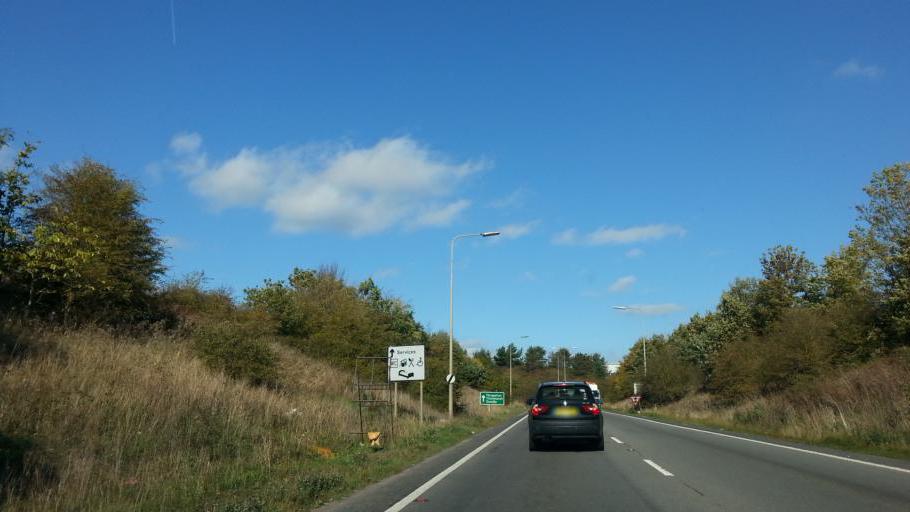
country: GB
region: England
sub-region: Northamptonshire
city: Thrapston
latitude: 52.3895
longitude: -0.5235
